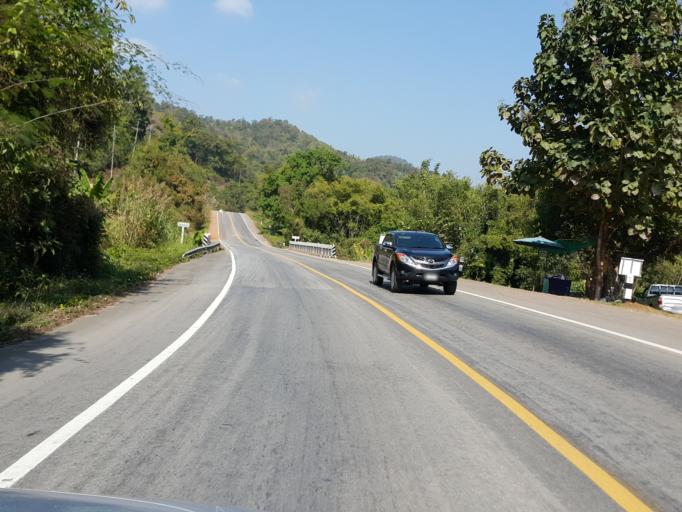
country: TH
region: Lampang
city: Wang Nuea
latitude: 19.1018
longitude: 99.4499
